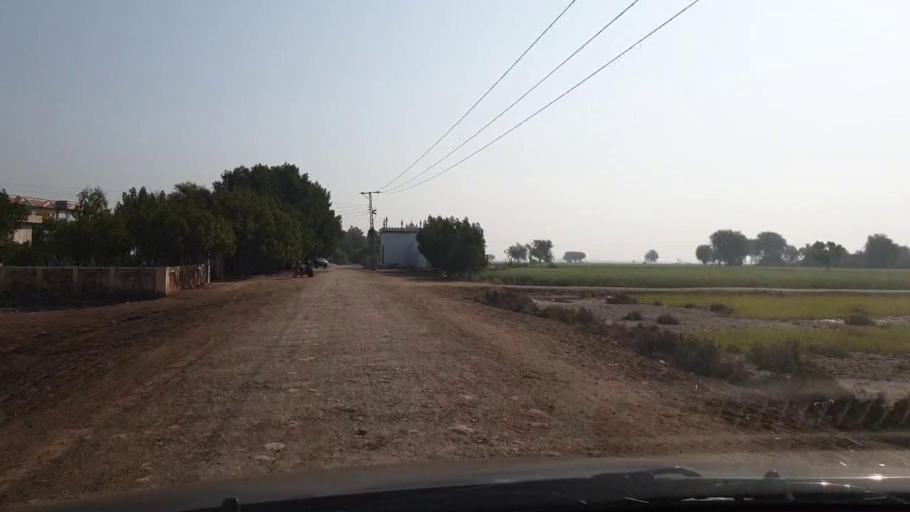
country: PK
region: Sindh
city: Sanghar
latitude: 25.9772
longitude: 68.9754
